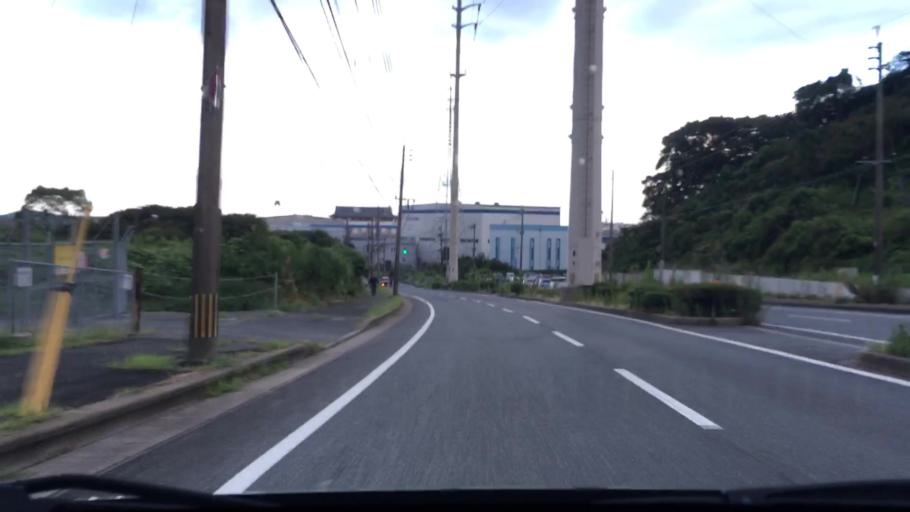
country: JP
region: Yamaguchi
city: Shimonoseki
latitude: 33.8868
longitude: 130.9827
